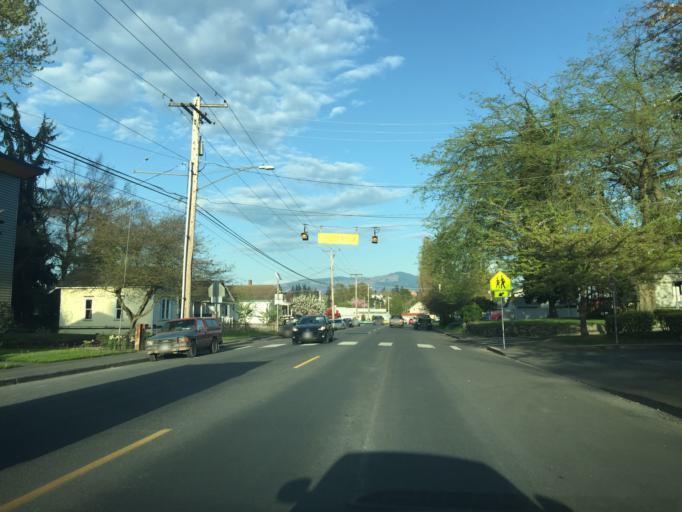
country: US
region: Washington
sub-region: Skagit County
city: Mount Vernon
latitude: 48.4208
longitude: -122.3487
